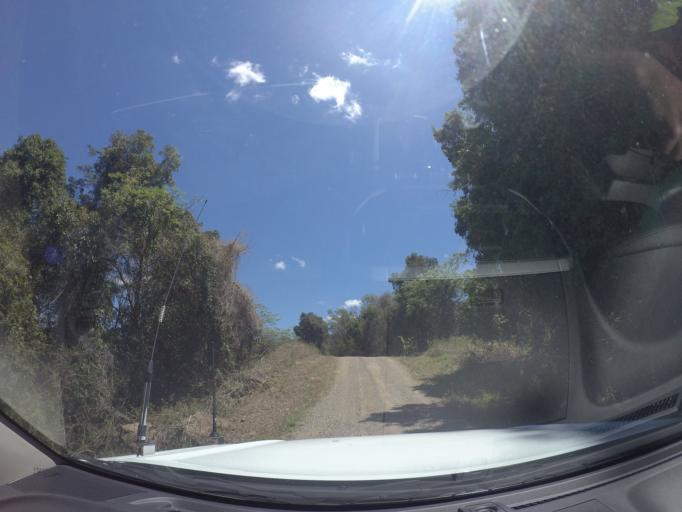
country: AU
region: Queensland
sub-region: Ipswich
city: Deebing Heights
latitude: -27.8291
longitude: 152.8179
